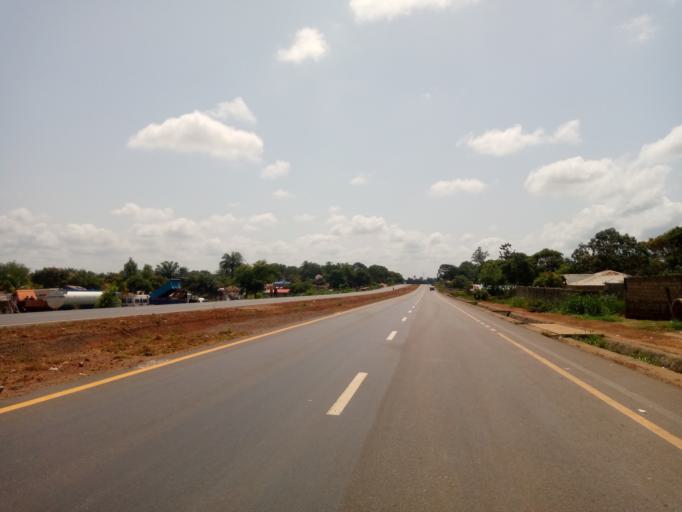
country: SL
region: Western Area
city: Waterloo
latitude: 8.3589
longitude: -12.9712
